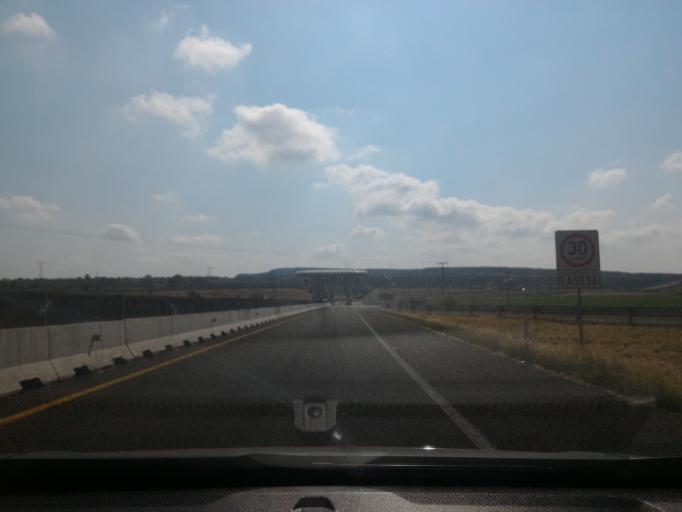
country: MX
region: Guanajuato
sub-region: Penjamo
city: Estacion la Piedad
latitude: 20.3948
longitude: -101.9996
